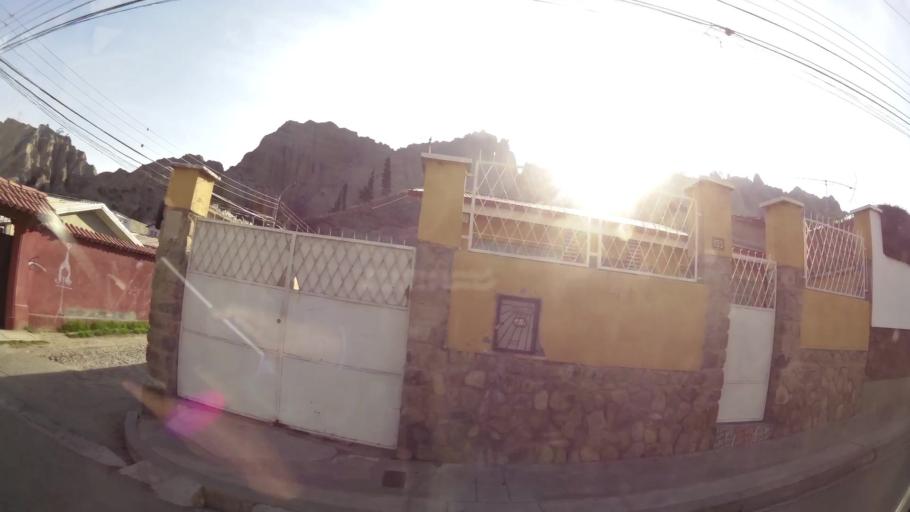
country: BO
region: La Paz
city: La Paz
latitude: -16.5180
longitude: -68.0904
